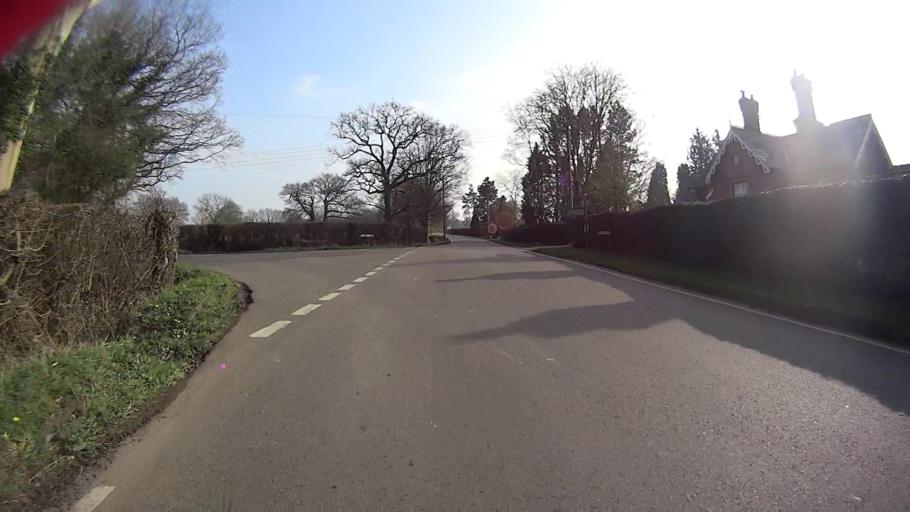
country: GB
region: England
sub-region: Surrey
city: Felbridge
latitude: 51.1764
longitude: -0.0653
